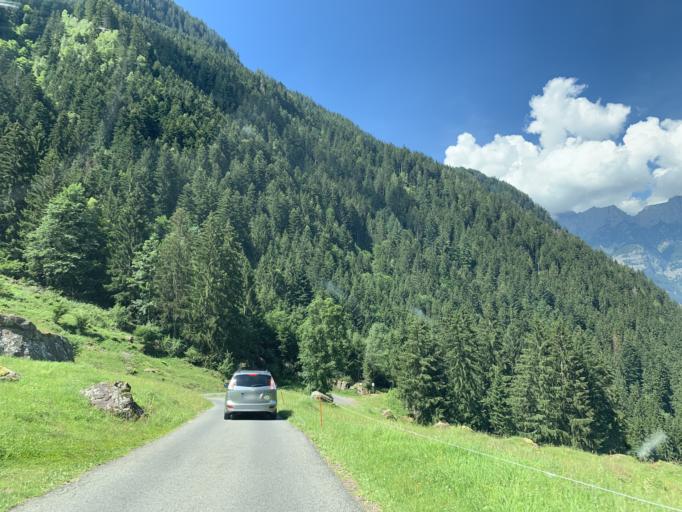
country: CH
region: Saint Gallen
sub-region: Wahlkreis Sarganserland
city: Quarten
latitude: 47.0858
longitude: 9.2023
